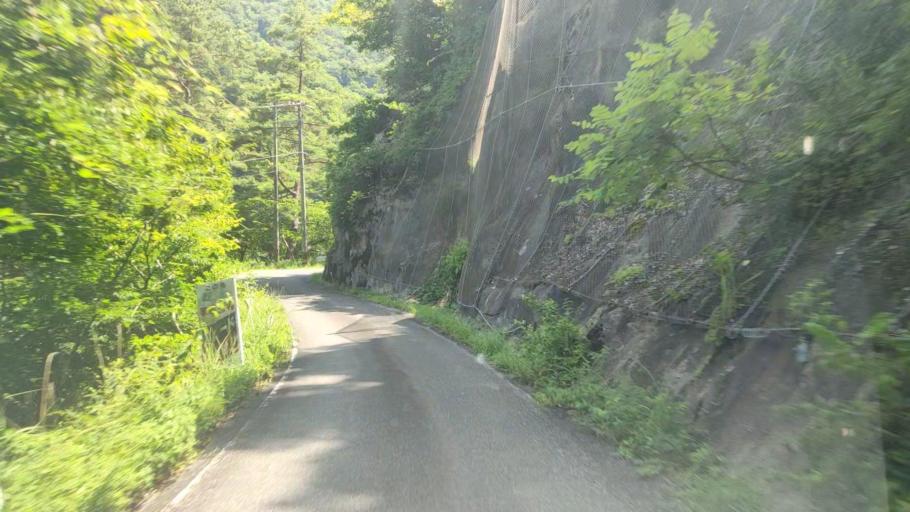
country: JP
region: Gifu
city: Godo
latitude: 35.6911
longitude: 136.5850
